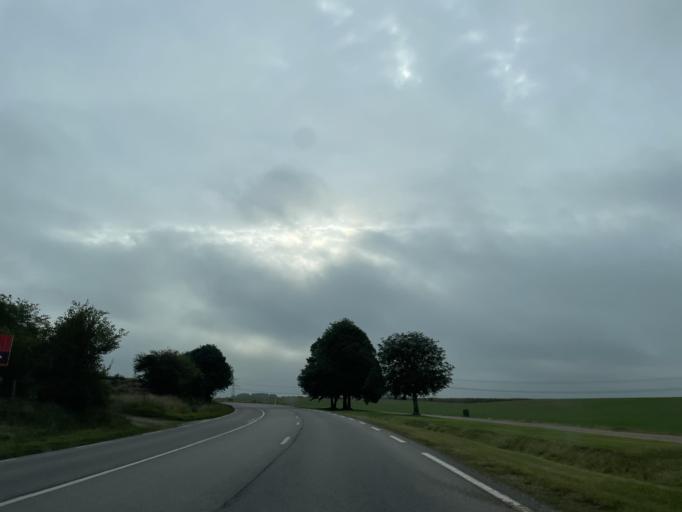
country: FR
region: Haute-Normandie
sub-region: Departement de la Seine-Maritime
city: Criel-sur-Mer
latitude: 50.0194
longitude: 1.3516
